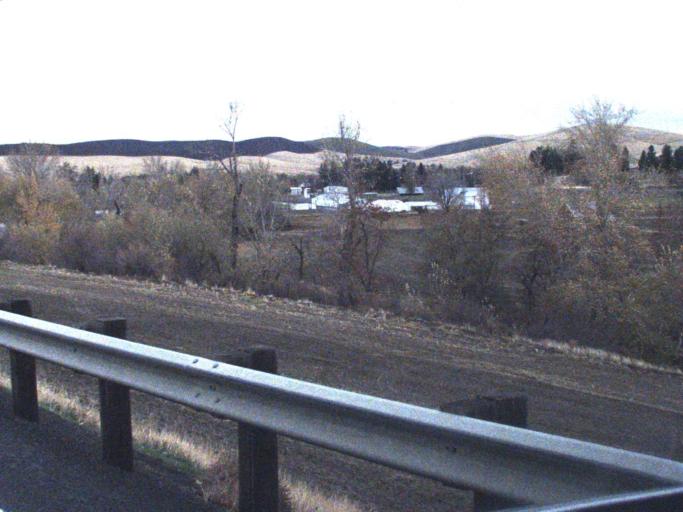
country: US
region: Washington
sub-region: Walla Walla County
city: Waitsburg
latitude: 46.2569
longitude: -118.1518
